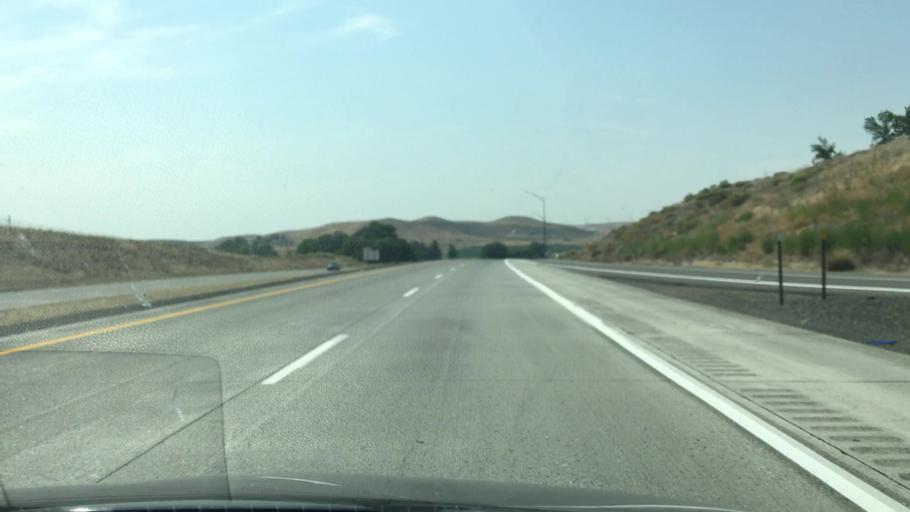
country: US
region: Idaho
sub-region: Elmore County
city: Glenns Ferry
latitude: 42.9600
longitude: -115.2952
